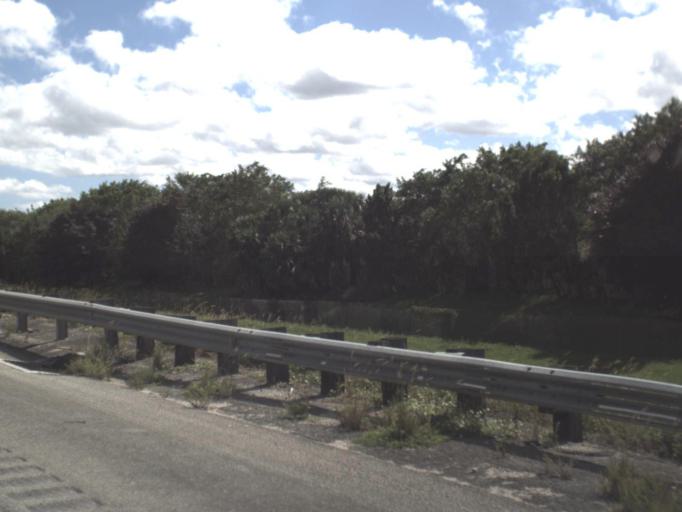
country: US
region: Florida
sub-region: Miami-Dade County
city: Country Club
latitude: 25.9706
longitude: -80.3139
